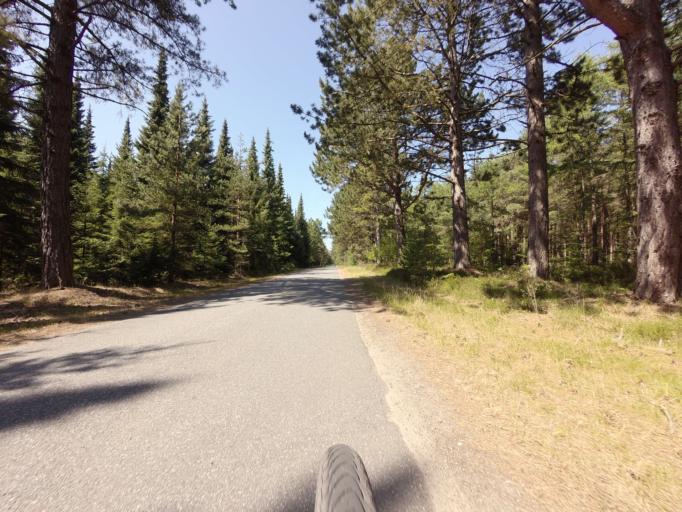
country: DK
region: North Denmark
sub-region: Laeso Kommune
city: Byrum
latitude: 57.2831
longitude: 11.0078
